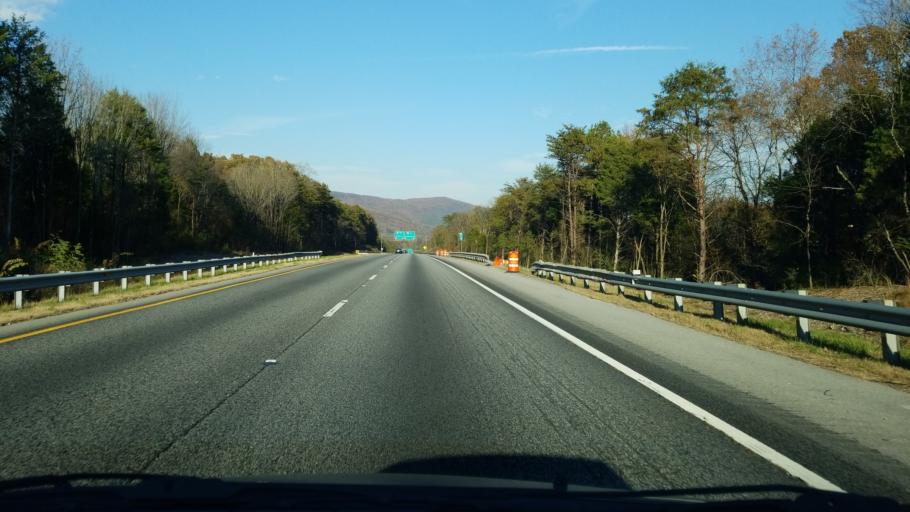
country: US
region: Georgia
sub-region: Dade County
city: Trenton
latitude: 34.9601
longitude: -85.4584
